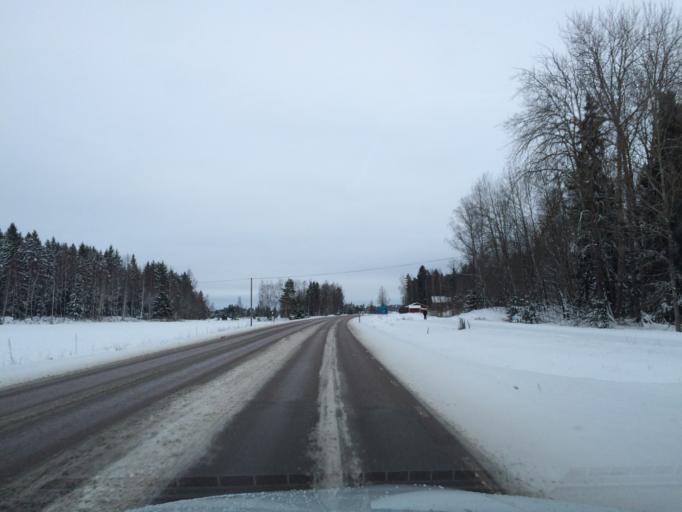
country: SE
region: Vaestmanland
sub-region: Hallstahammars Kommun
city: Hallstahammar
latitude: 59.5983
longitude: 16.2499
